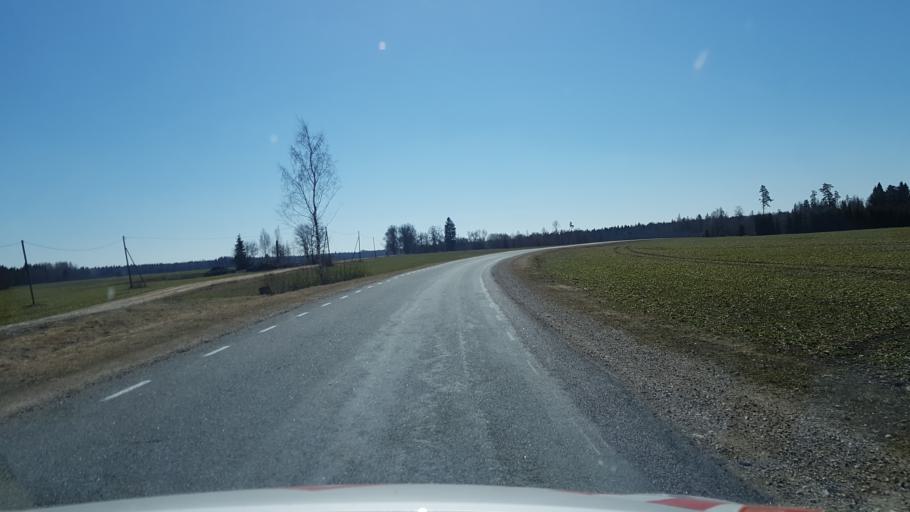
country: EE
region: Laeaene-Virumaa
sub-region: Rakke vald
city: Rakke
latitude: 59.0230
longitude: 26.3532
